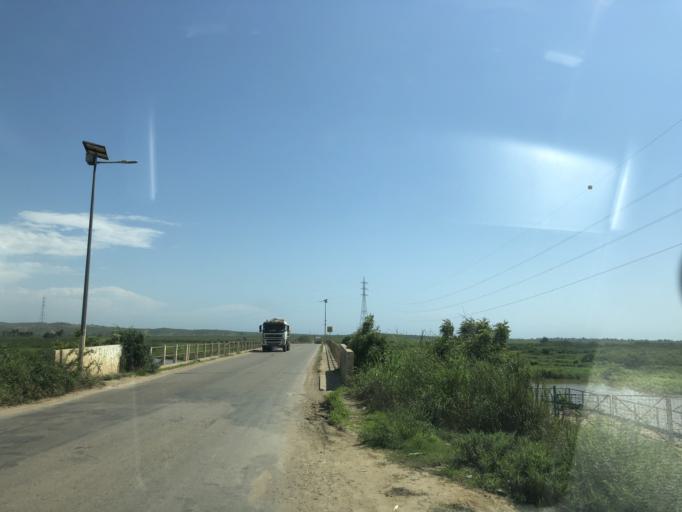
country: AO
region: Cuanza Sul
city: Sumbe
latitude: -10.8730
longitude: 13.8405
